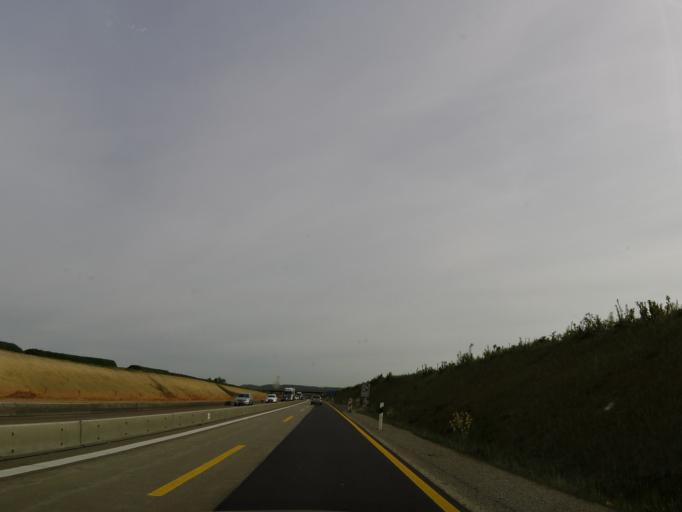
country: DE
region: Lower Saxony
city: Bockenem
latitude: 51.9852
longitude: 10.1543
